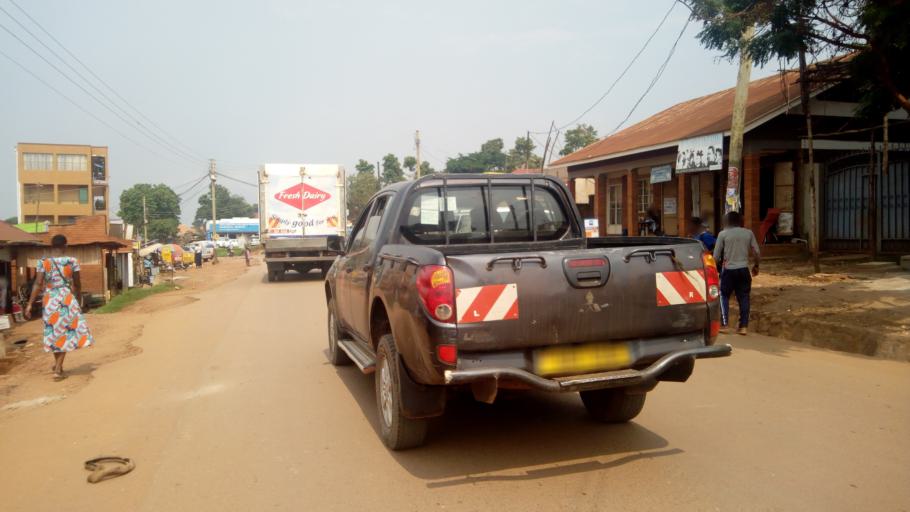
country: UG
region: Central Region
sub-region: Wakiso District
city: Kireka
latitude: 0.3209
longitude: 32.6449
